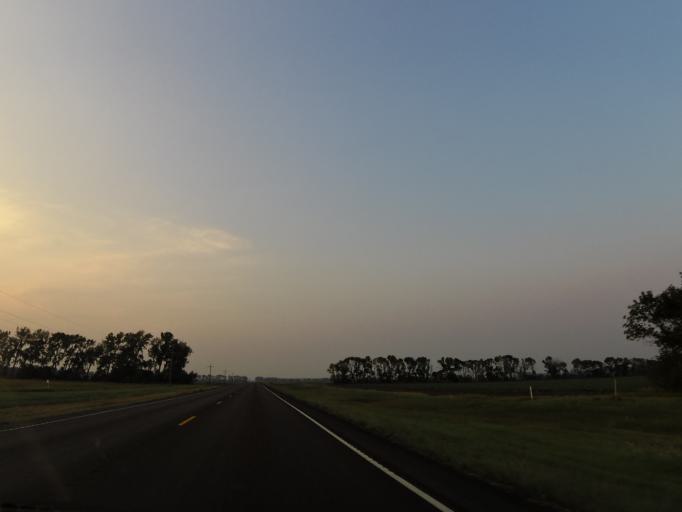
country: US
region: North Dakota
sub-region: Walsh County
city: Park River
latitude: 48.3443
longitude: -97.6225
